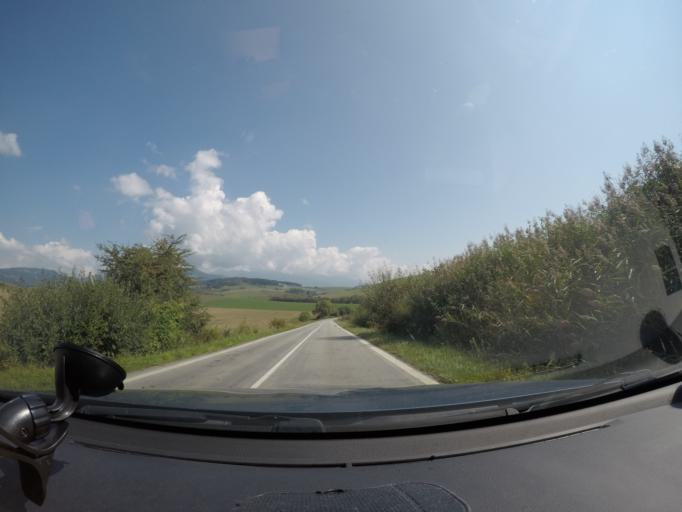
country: SK
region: Zilinsky
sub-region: Okres Liptovsky Mikulas
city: Liptovsky Mikulas
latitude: 49.1321
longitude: 19.5273
